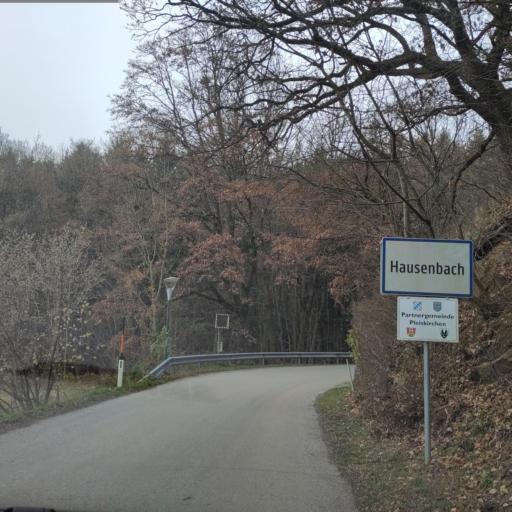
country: AT
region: Lower Austria
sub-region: Politischer Bezirk Sankt Polten
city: Neidling
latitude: 48.2430
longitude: 15.5501
